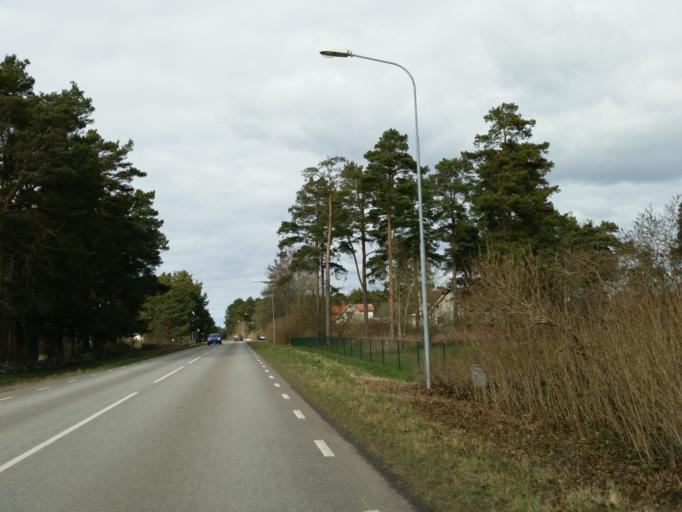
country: SE
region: Kalmar
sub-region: Morbylanga Kommun
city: Sodra Sandby
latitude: 56.6060
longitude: 16.6448
